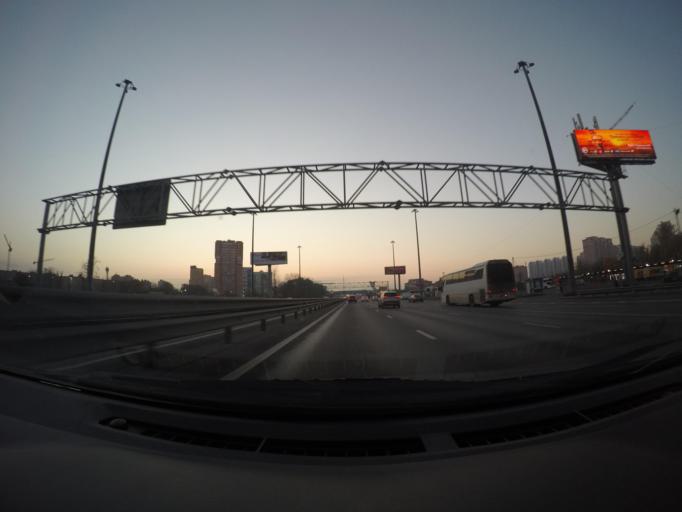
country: RU
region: Moscow
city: Zhulebino
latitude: 55.6735
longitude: 37.8621
